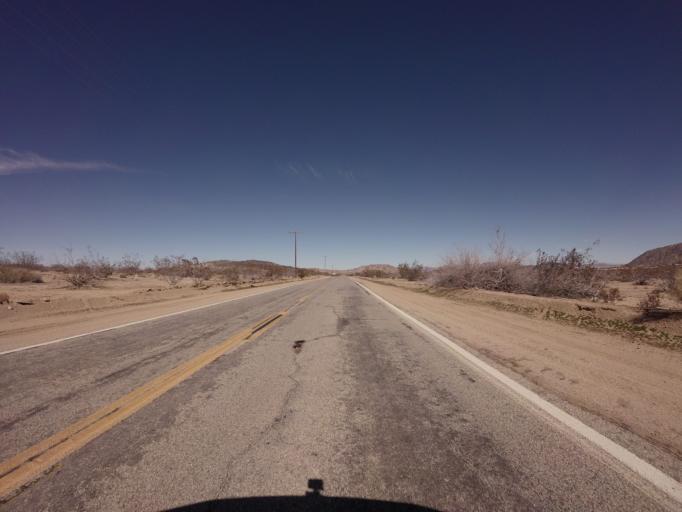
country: US
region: California
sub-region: San Bernardino County
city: Yucca Valley
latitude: 34.2811
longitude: -116.4044
